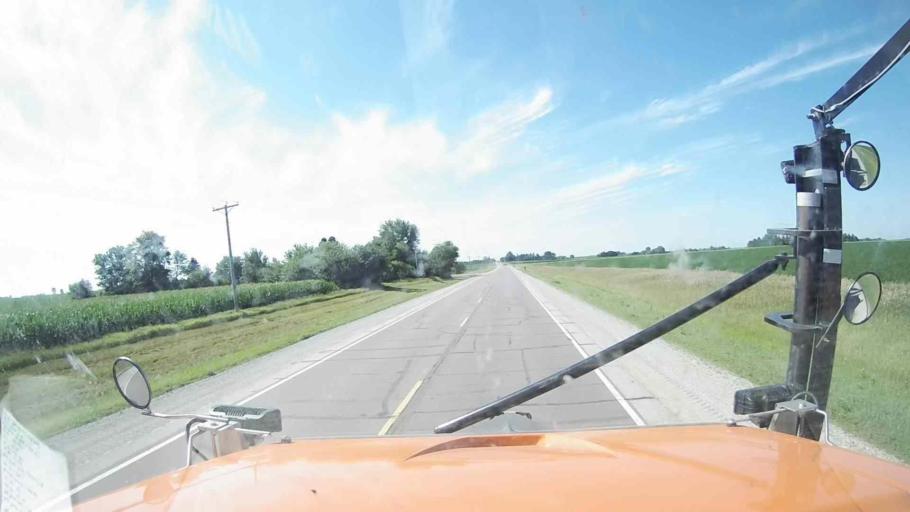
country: US
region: Iowa
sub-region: Cerro Gordo County
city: Mason City
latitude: 43.0872
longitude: -93.2015
